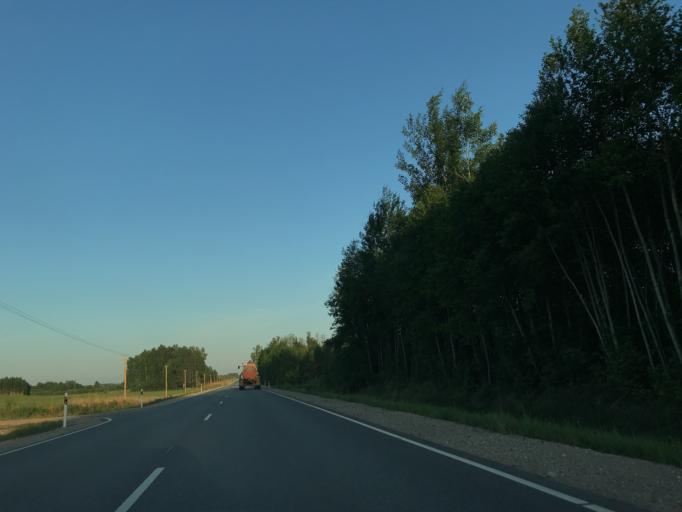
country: LV
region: Vecumnieki
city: Vecumnieki
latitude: 56.5252
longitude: 24.6825
